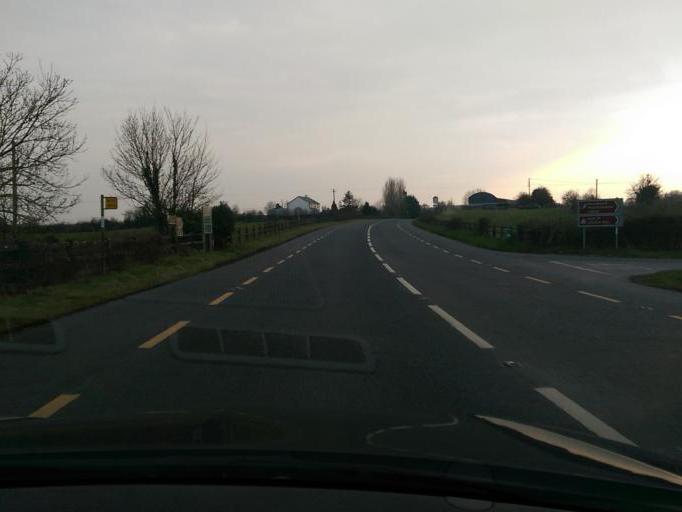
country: IE
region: Leinster
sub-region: An Longfort
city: Ballymahon
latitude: 53.5105
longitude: -7.8261
